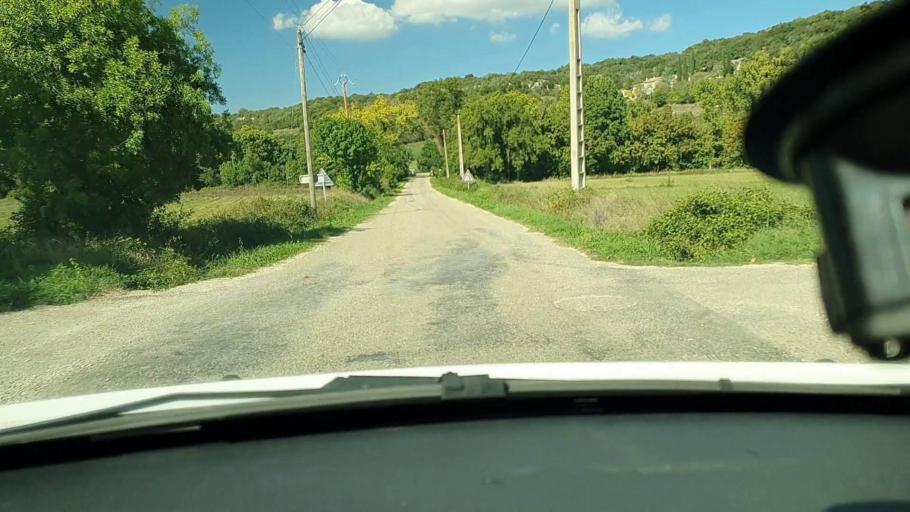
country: FR
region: Languedoc-Roussillon
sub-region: Departement du Gard
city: Goudargues
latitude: 44.1713
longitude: 4.3855
